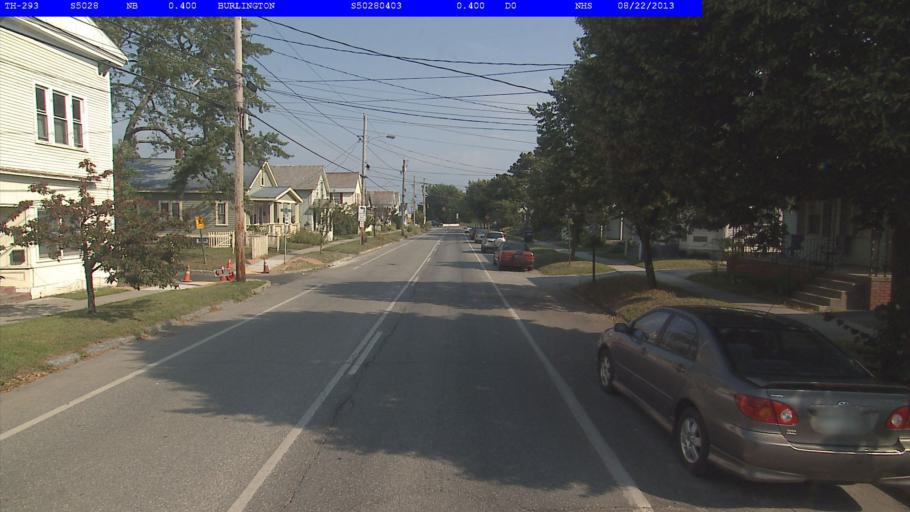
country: US
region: Vermont
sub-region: Chittenden County
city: Burlington
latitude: 44.4861
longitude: -73.2178
